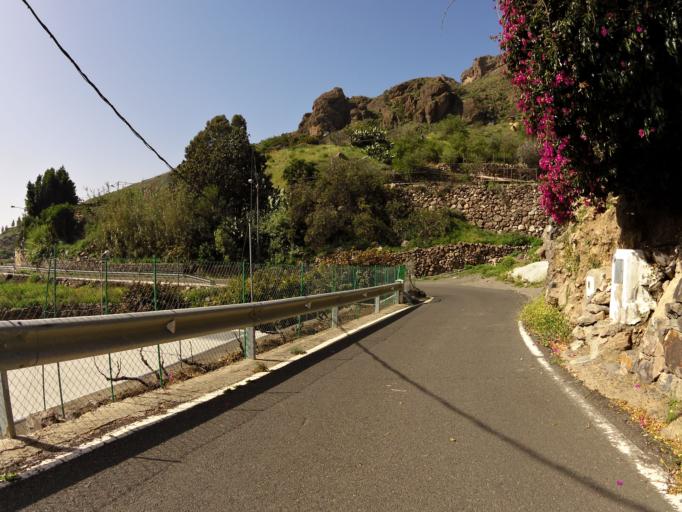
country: ES
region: Canary Islands
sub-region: Provincia de Las Palmas
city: Mogan
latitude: 27.9128
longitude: -15.6674
